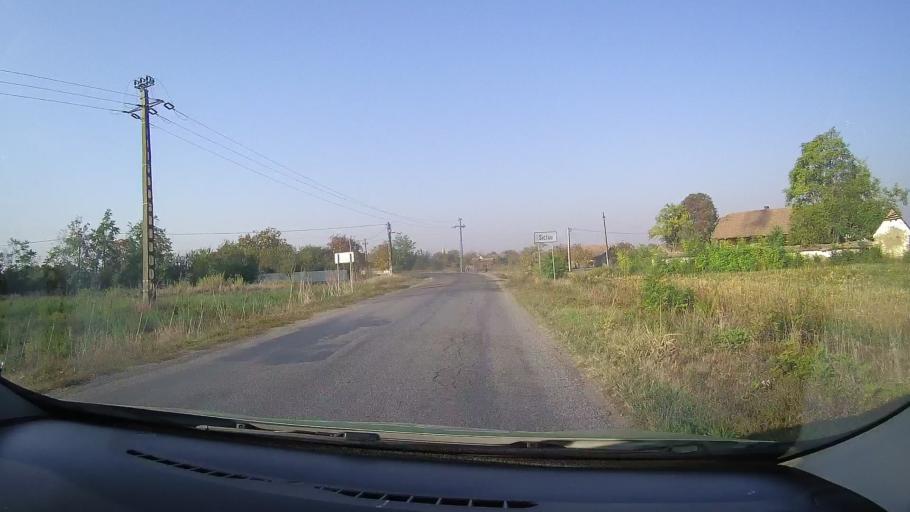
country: RO
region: Arad
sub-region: Comuna Graniceri
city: Siclau
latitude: 46.4952
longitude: 21.3725
